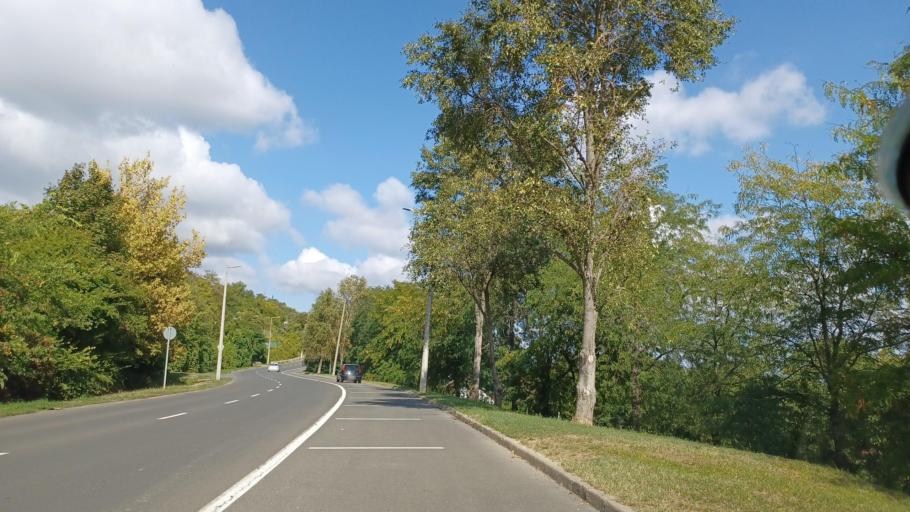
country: HU
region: Tolna
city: Szekszard
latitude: 46.3389
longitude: 18.6972
